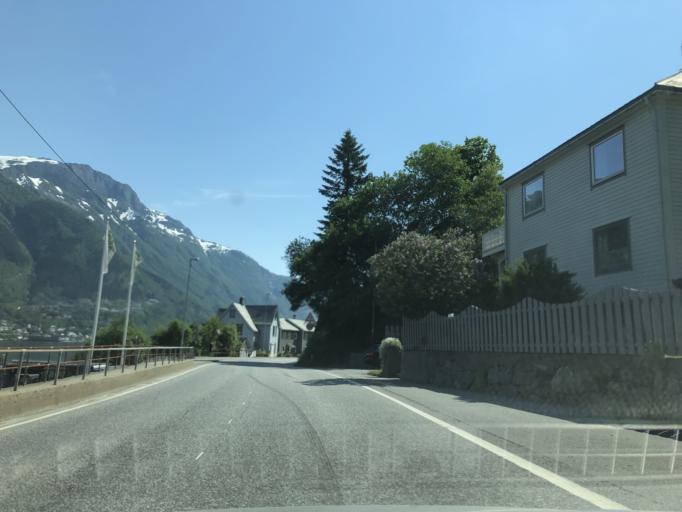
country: NO
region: Hordaland
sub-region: Odda
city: Odda
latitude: 60.0836
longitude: 6.5304
